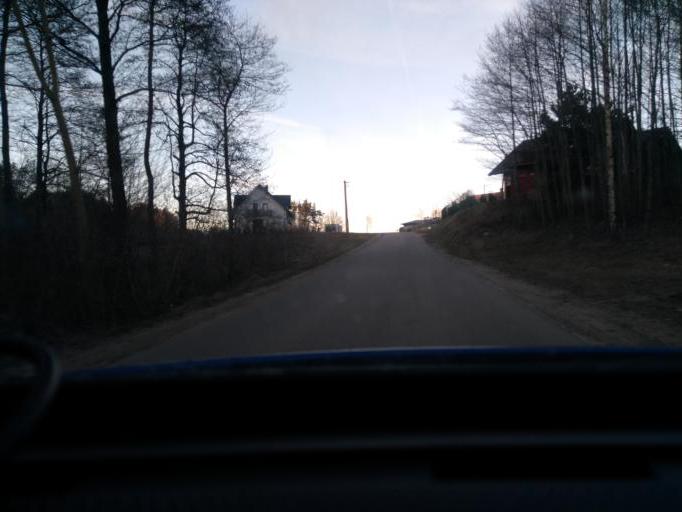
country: PL
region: Pomeranian Voivodeship
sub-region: Powiat kartuski
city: Przodkowo
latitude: 54.3853
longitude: 18.2695
